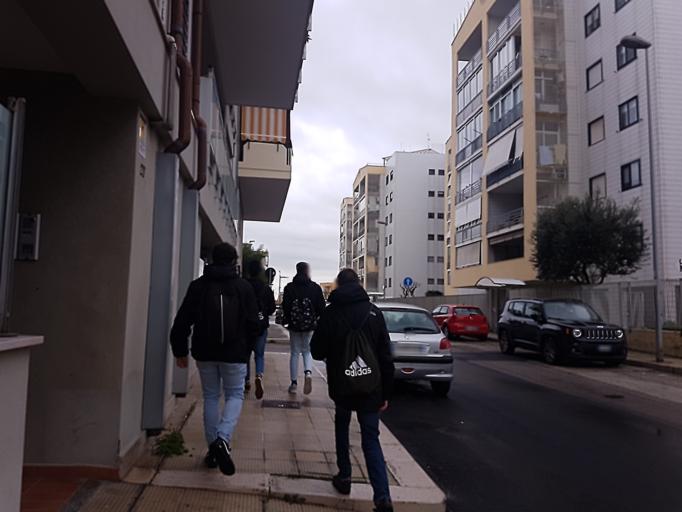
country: IT
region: Apulia
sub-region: Provincia di Bari
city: San Paolo
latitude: 41.1389
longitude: 16.8103
